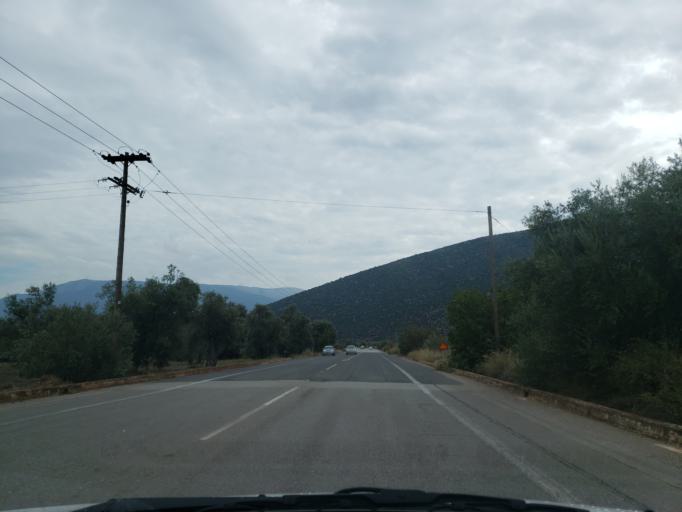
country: GR
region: Central Greece
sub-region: Nomos Fokidos
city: Itea
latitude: 38.4869
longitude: 22.4199
